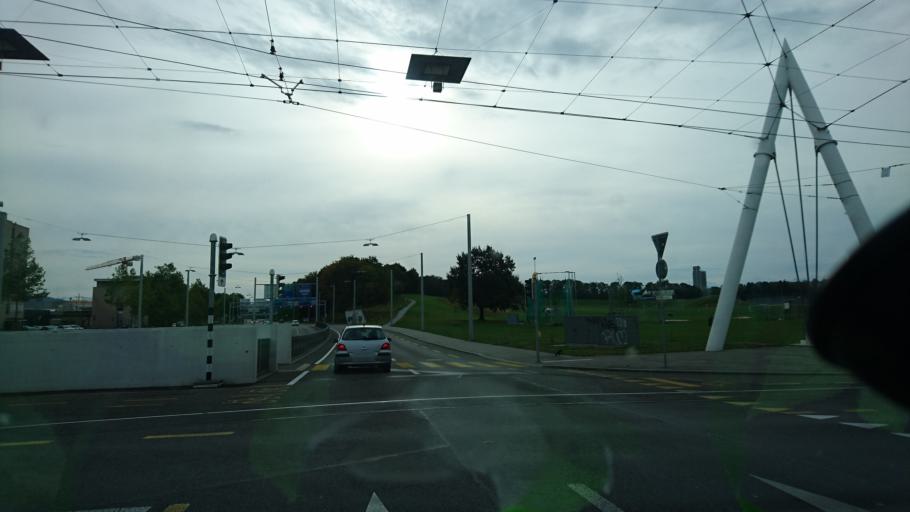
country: CH
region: Bern
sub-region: Bern-Mittelland District
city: Bern
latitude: 46.9648
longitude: 7.4681
